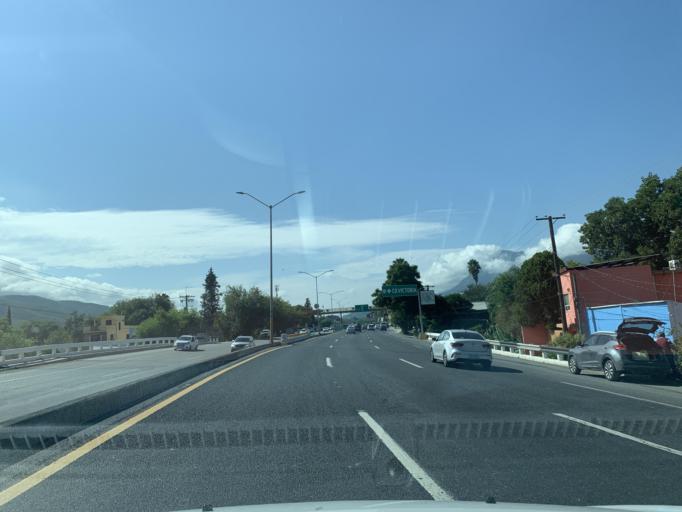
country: MX
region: Nuevo Leon
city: Santiago
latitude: 25.4088
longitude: -100.1359
